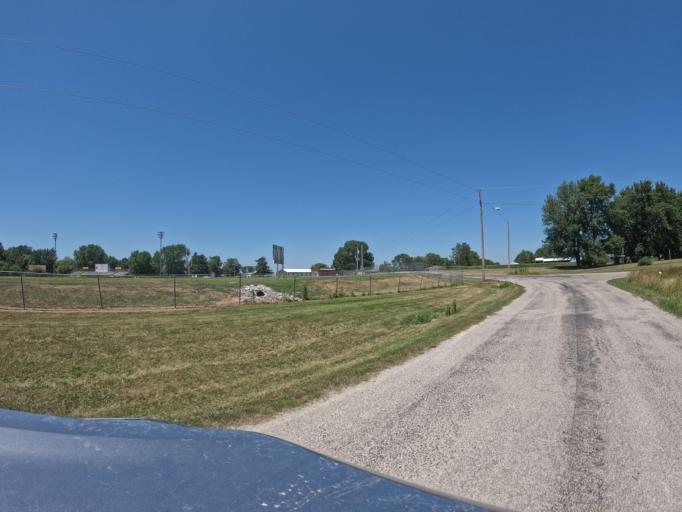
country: US
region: Iowa
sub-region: Keokuk County
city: Sigourney
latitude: 41.4548
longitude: -92.3315
